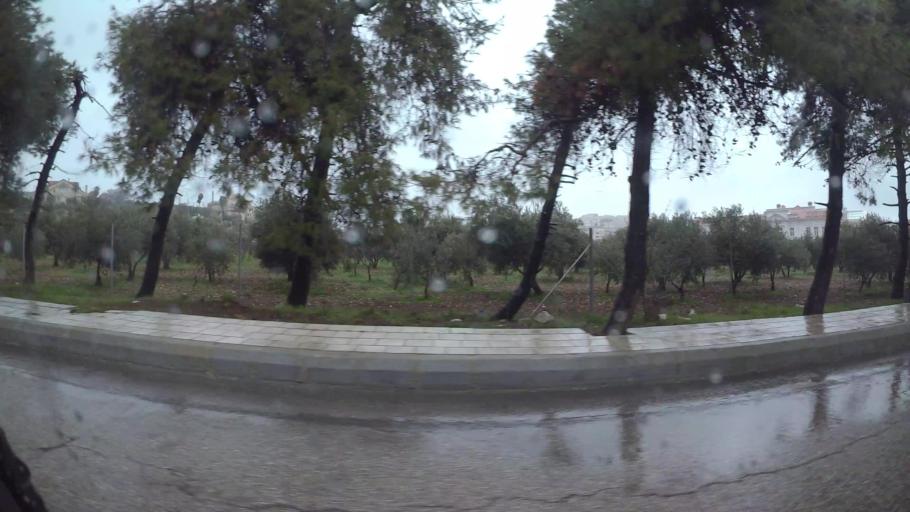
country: JO
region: Amman
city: Wadi as Sir
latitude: 31.9954
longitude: 35.8141
